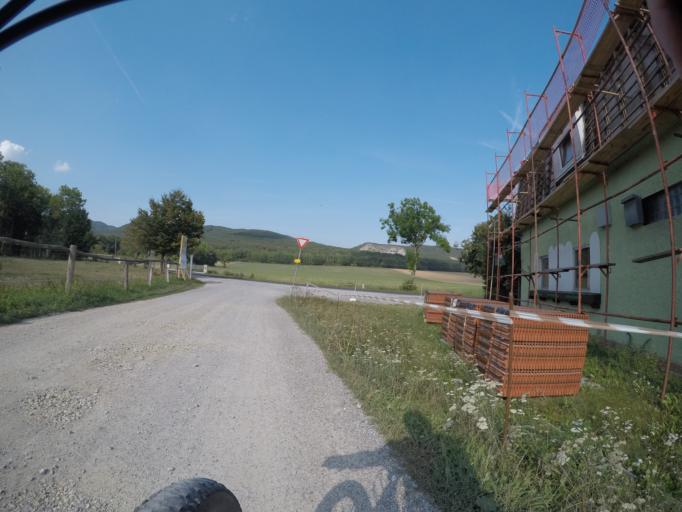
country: AT
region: Lower Austria
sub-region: Politischer Bezirk Baden
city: Berndorf
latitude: 47.9689
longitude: 16.1445
